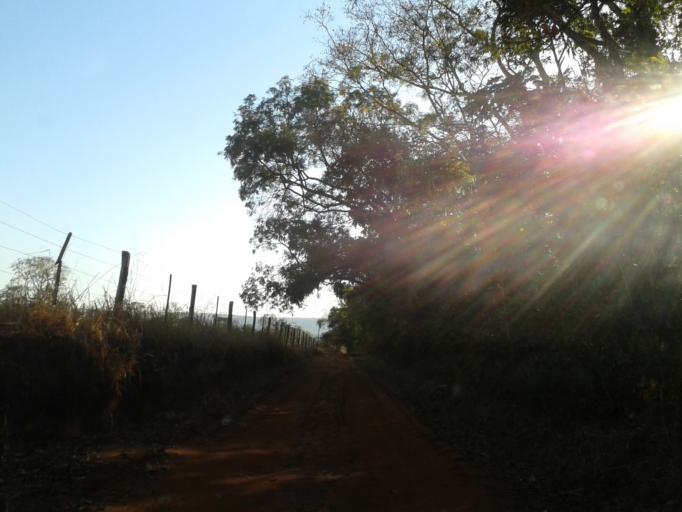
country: BR
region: Minas Gerais
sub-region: Santa Vitoria
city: Santa Vitoria
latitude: -19.1810
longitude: -50.0263
